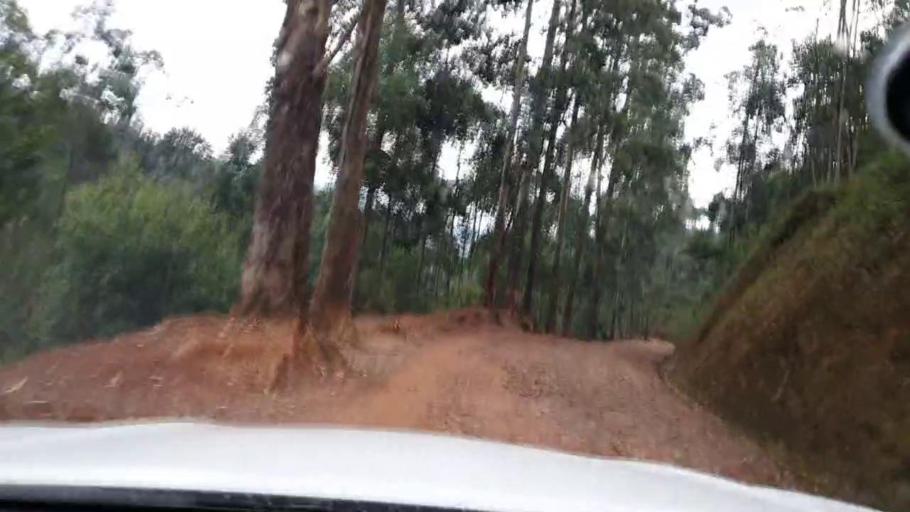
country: RW
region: Western Province
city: Cyangugu
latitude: -2.4086
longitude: 29.2064
